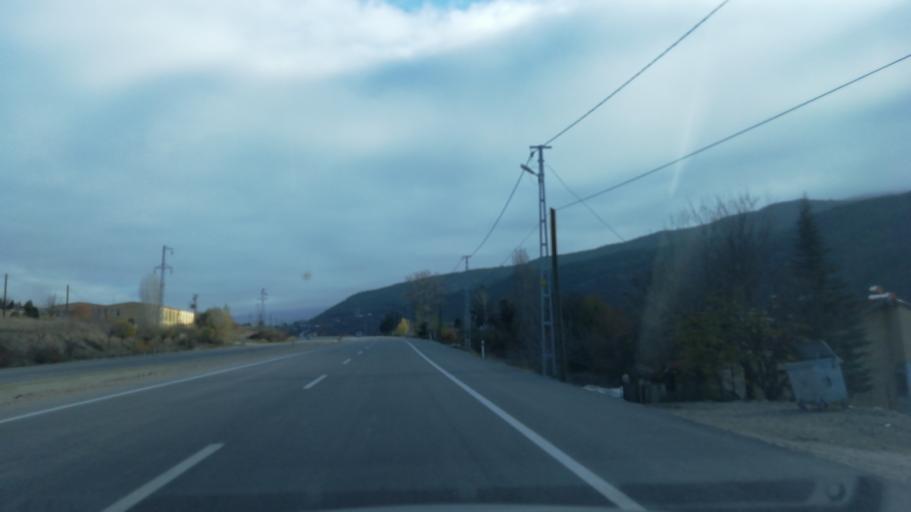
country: TR
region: Karabuk
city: Safranbolu
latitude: 41.2172
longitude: 32.7499
